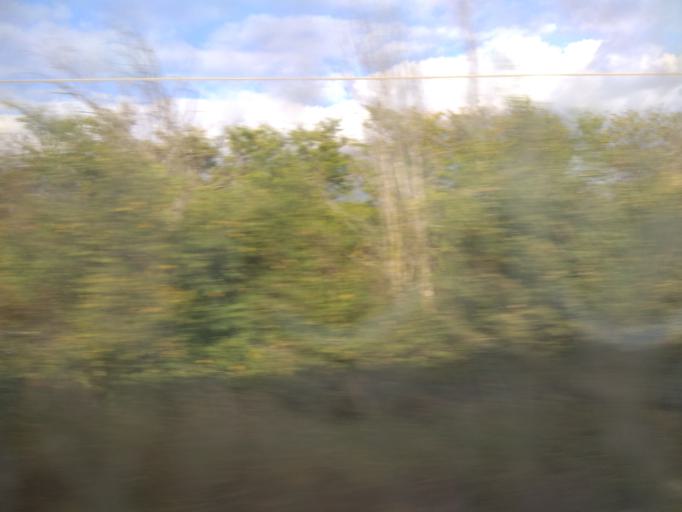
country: IT
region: Latium
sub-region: Citta metropolitana di Roma Capitale
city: Maccarese
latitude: 41.9096
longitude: 12.2066
